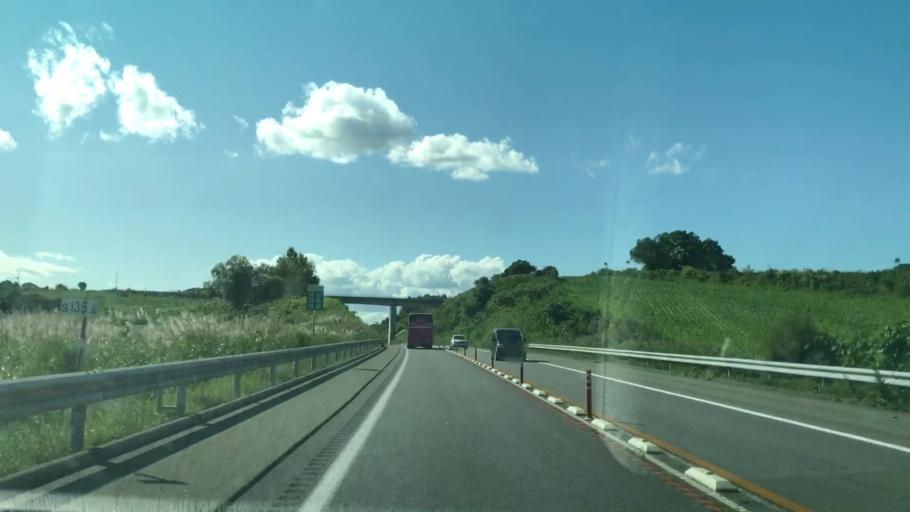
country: JP
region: Hokkaido
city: Date
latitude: 42.4965
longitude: 140.8681
